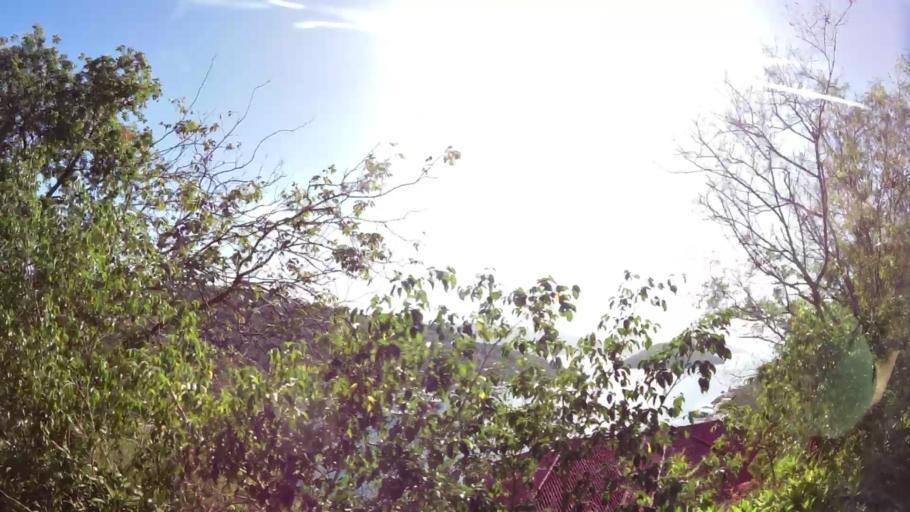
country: VG
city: Road Town
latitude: 18.3892
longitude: -64.6992
